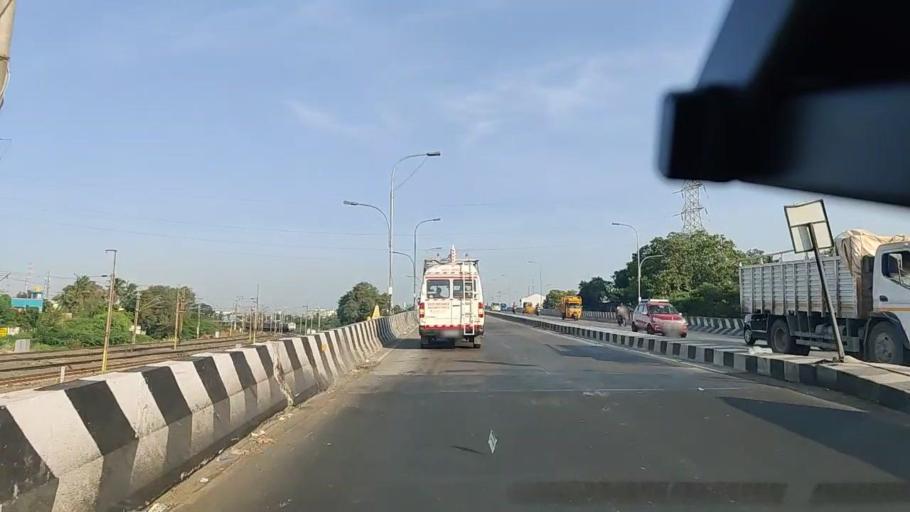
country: IN
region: Tamil Nadu
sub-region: Chennai
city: George Town
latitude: 13.1076
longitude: 80.2687
